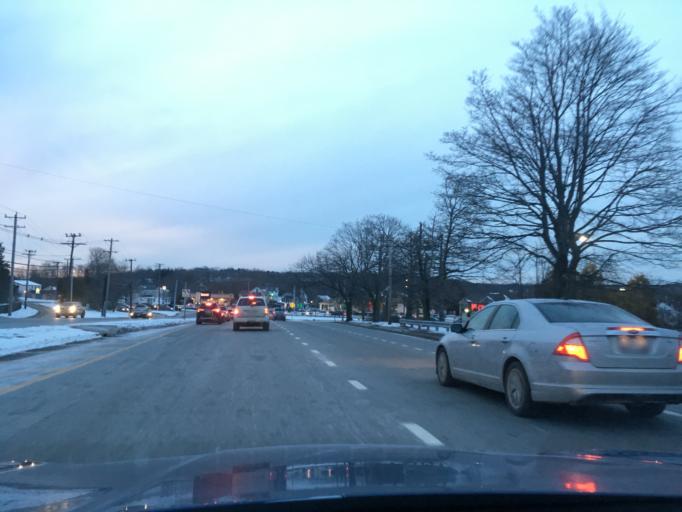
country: US
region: Rhode Island
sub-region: Kent County
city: West Warwick
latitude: 41.7186
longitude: -71.4830
